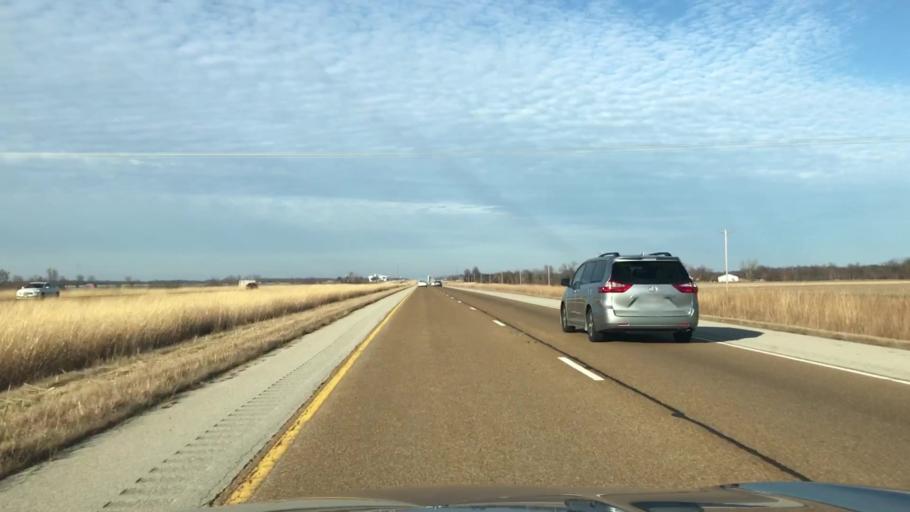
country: US
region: Illinois
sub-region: Montgomery County
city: Litchfield
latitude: 39.2409
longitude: -89.6411
